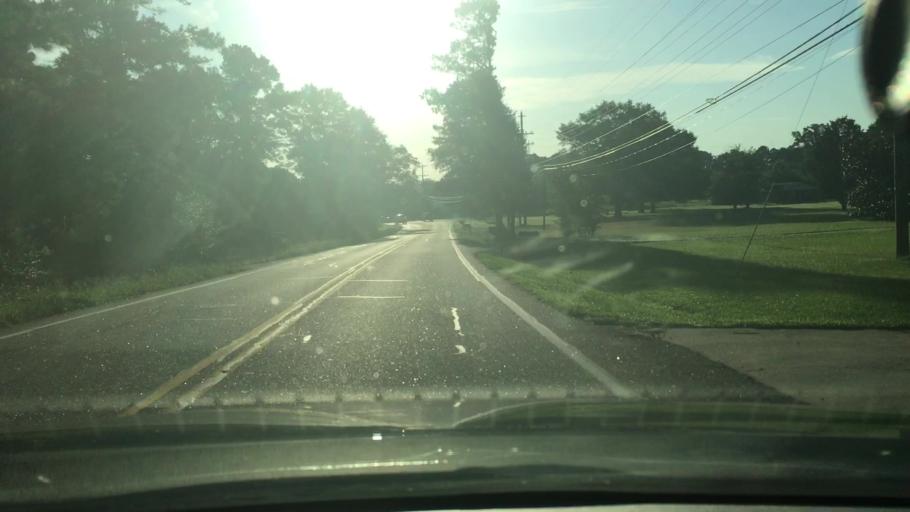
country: US
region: Georgia
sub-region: Fayette County
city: Peachtree City
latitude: 33.3805
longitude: -84.6750
